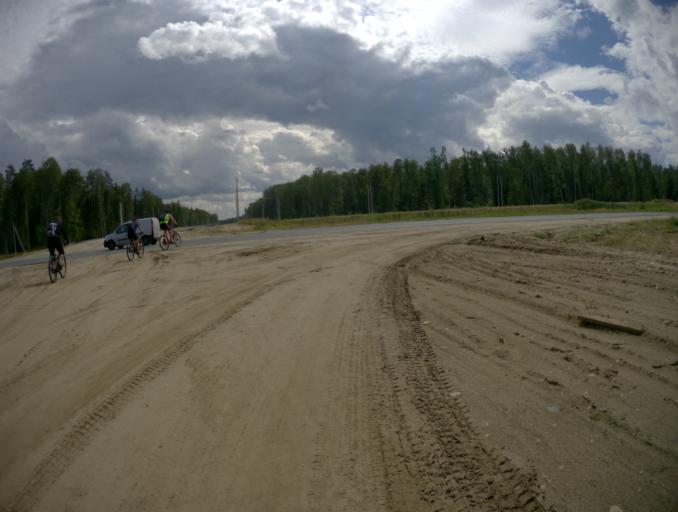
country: RU
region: Vladimir
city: Golovino
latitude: 56.0153
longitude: 40.5768
